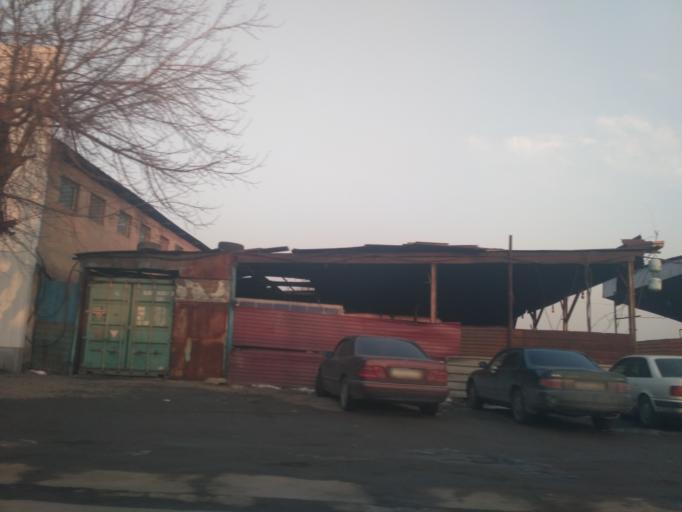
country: KZ
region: Almaty Qalasy
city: Almaty
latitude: 43.2644
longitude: 76.8680
